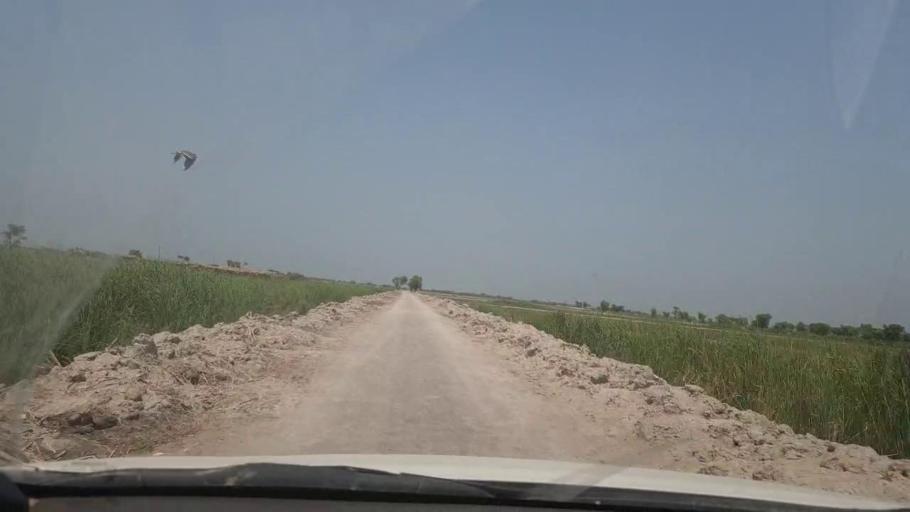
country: PK
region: Sindh
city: Lakhi
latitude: 27.8786
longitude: 68.7351
